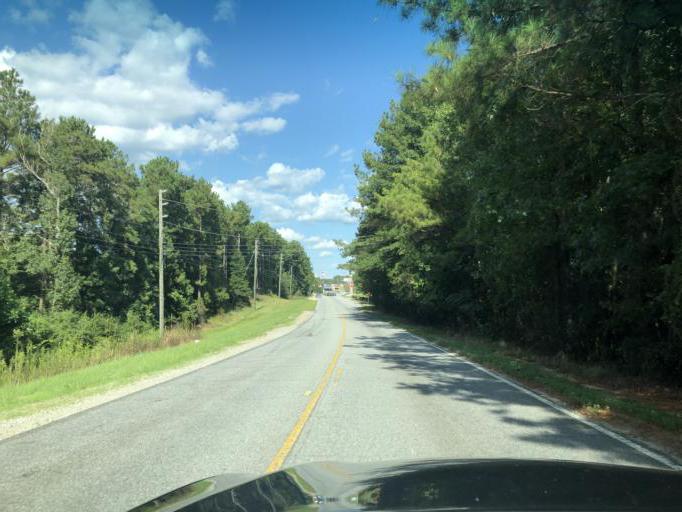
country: US
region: Georgia
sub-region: Muscogee County
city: Columbus
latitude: 32.5205
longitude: -84.8961
